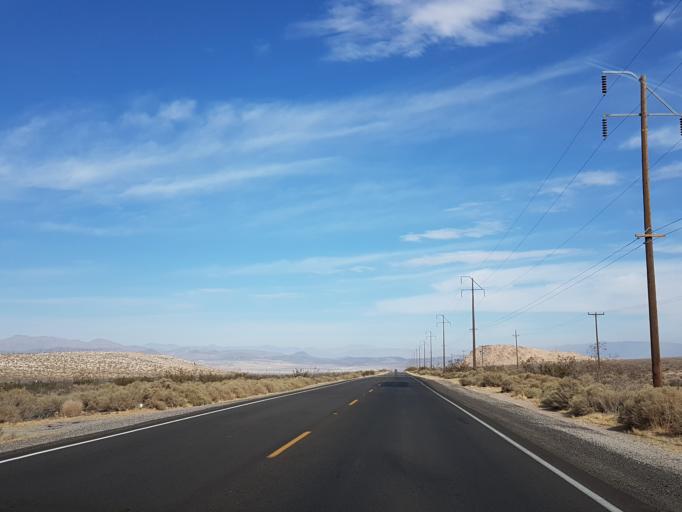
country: US
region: California
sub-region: Kern County
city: Ridgecrest
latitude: 35.6261
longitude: -117.5909
